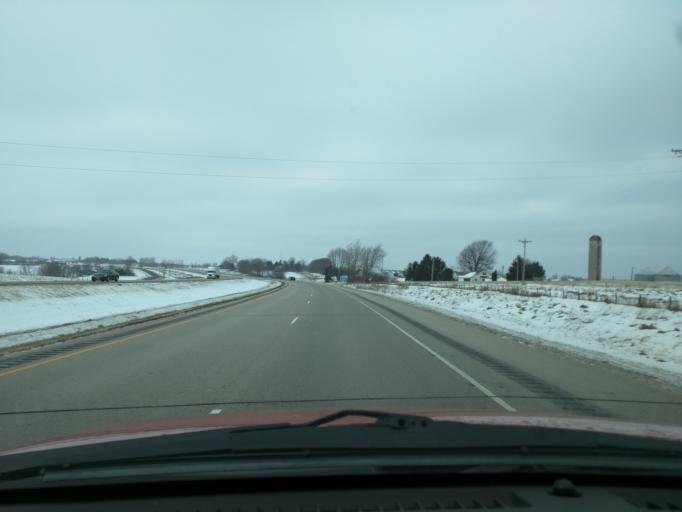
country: US
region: Wisconsin
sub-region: Trempealeau County
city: Trempealeau
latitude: 43.9258
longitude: -91.4756
